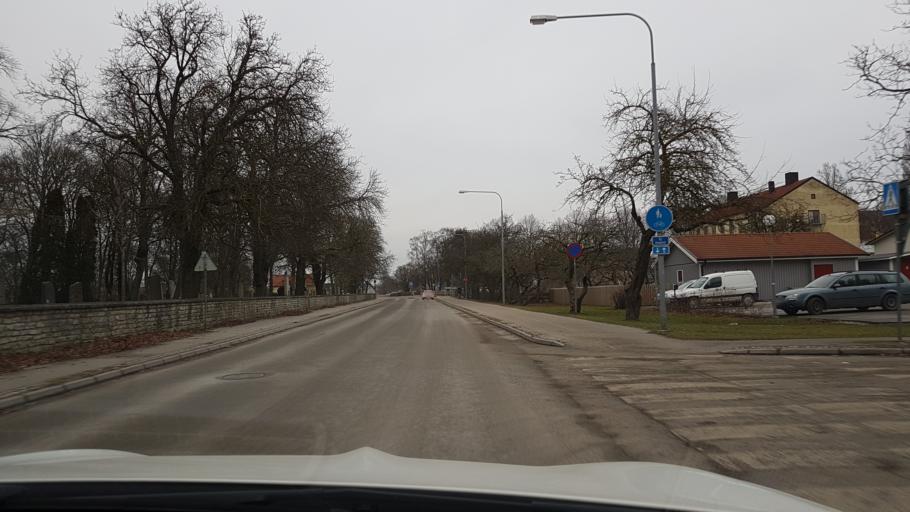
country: SE
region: Gotland
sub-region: Gotland
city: Visby
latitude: 57.6320
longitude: 18.2973
